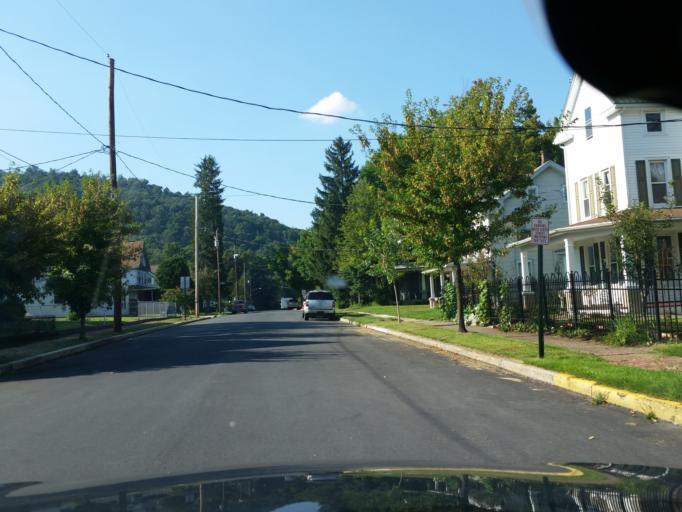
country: US
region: Pennsylvania
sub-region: Perry County
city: Marysville
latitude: 40.3467
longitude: -76.9326
